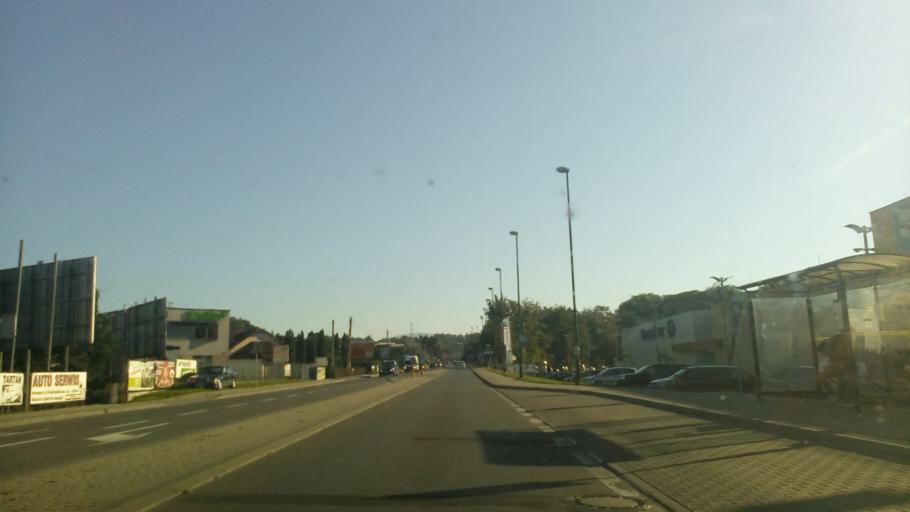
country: PL
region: Lesser Poland Voivodeship
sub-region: Powiat nowosadecki
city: Nowy Sacz
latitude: 49.5866
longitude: 20.6737
